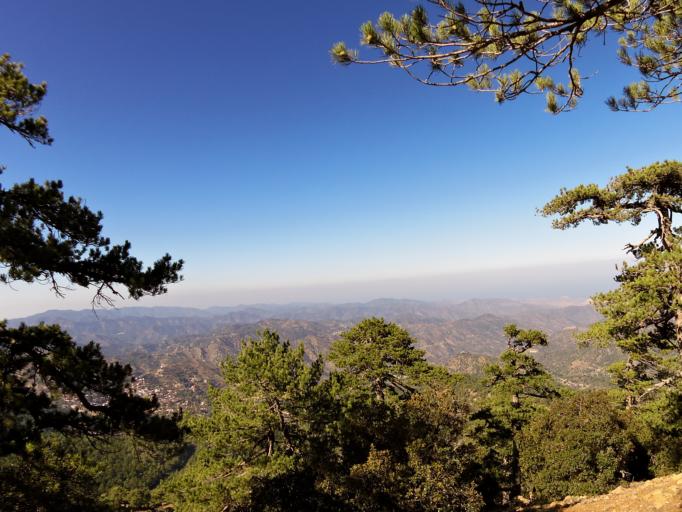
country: CY
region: Lefkosia
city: Kakopetria
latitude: 34.9587
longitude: 32.8545
